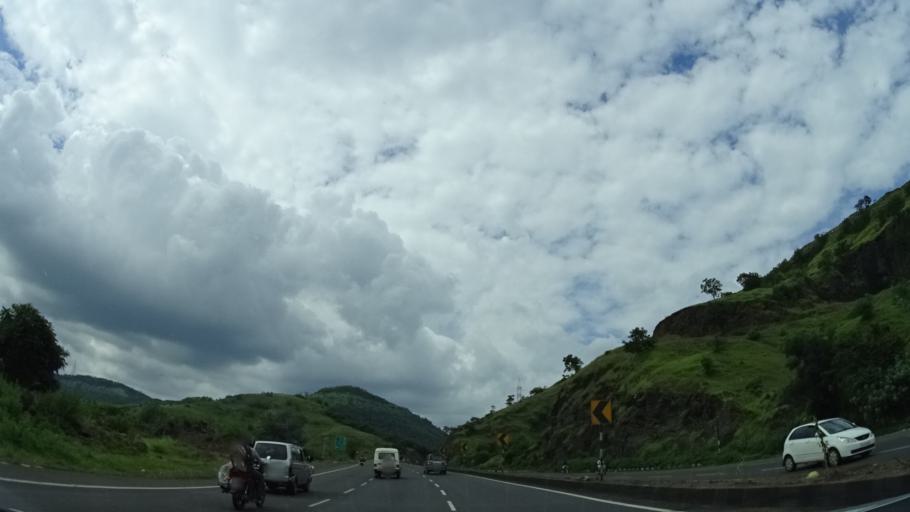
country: IN
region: Maharashtra
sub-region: Satara Division
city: Satara
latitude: 17.6515
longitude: 74.0139
